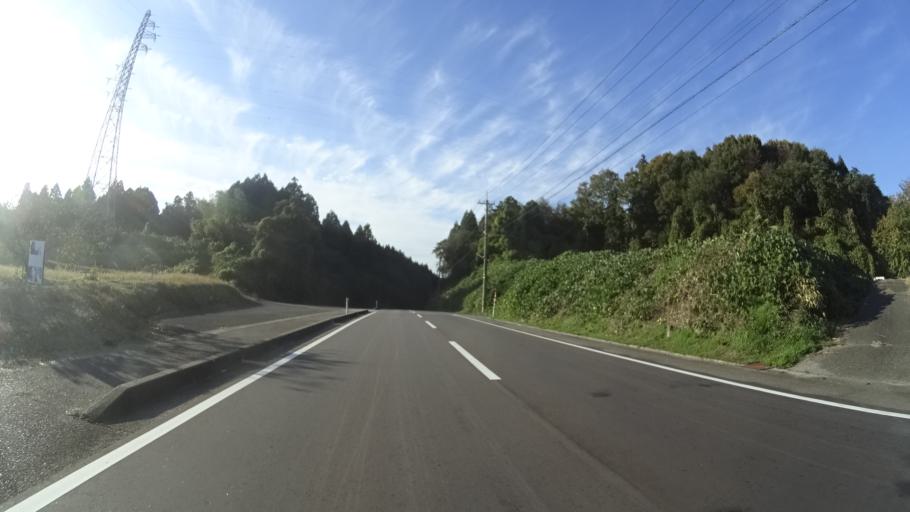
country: JP
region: Ishikawa
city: Hakui
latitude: 37.0058
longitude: 136.8031
